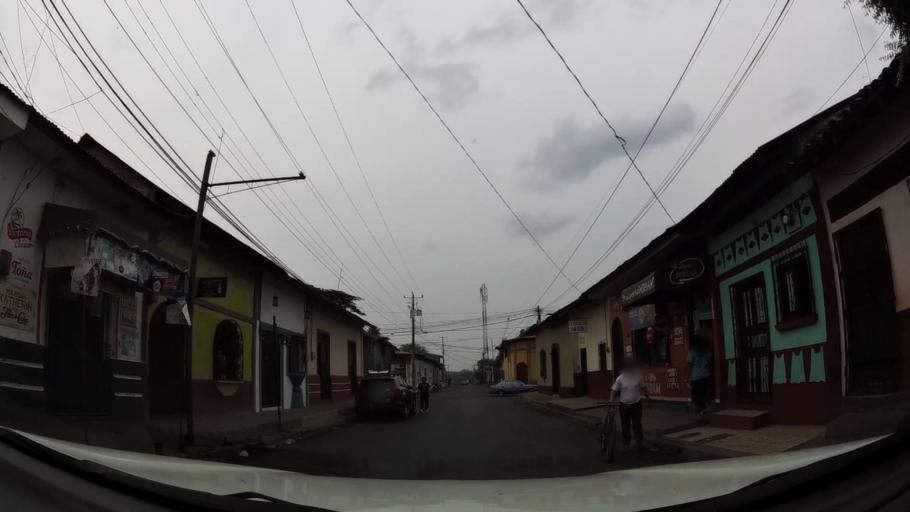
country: NI
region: Leon
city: Leon
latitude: 12.4382
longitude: -86.8715
